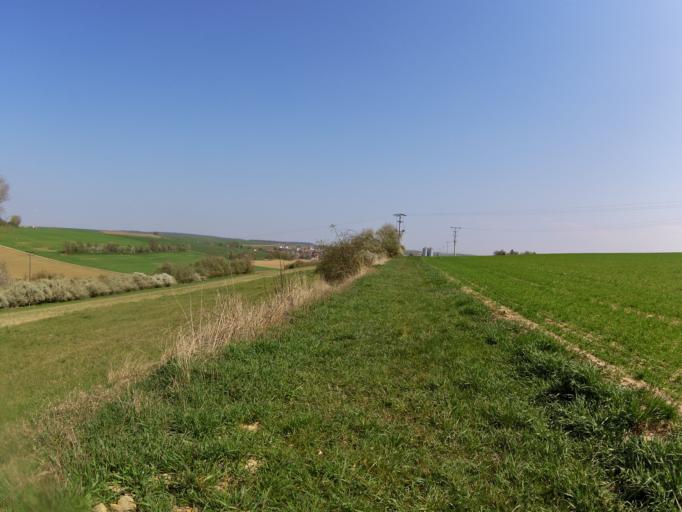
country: DE
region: Bavaria
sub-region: Regierungsbezirk Unterfranken
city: Mainstockheim
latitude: 49.8167
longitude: 10.1112
